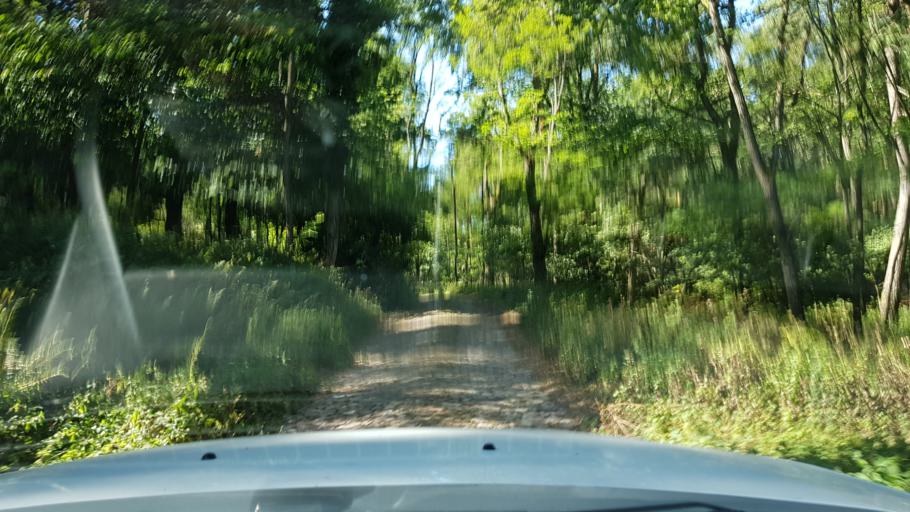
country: PL
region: West Pomeranian Voivodeship
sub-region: Powiat gryfinski
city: Cedynia
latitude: 52.8494
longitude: 14.2318
